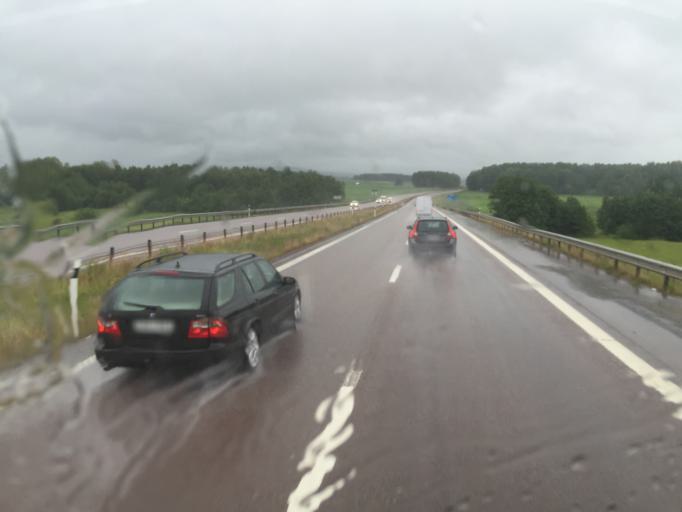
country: SE
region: Dalarna
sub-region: Borlange Kommun
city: Ornas
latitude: 60.5014
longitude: 15.5164
